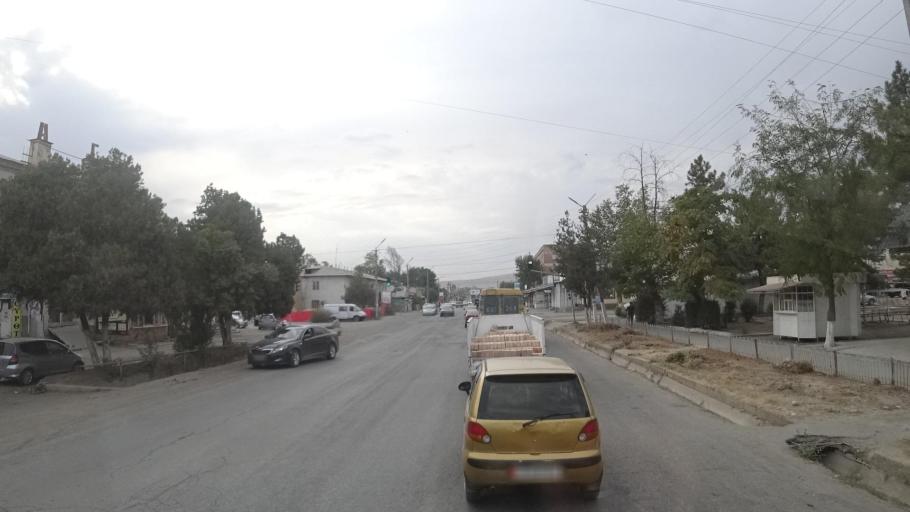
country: KG
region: Jalal-Abad
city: Massy
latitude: 41.0649
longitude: 72.6360
